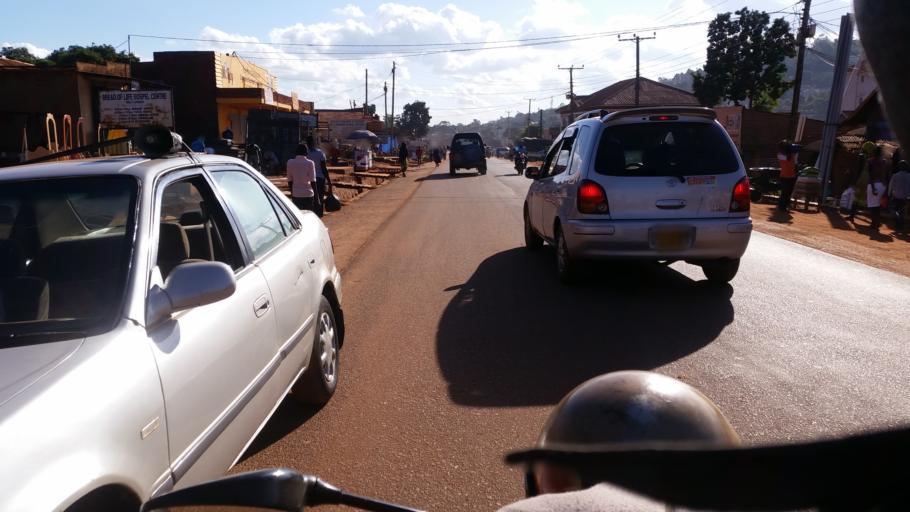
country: UG
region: Central Region
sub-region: Wakiso District
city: Kireka
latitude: 0.3218
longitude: 32.6412
